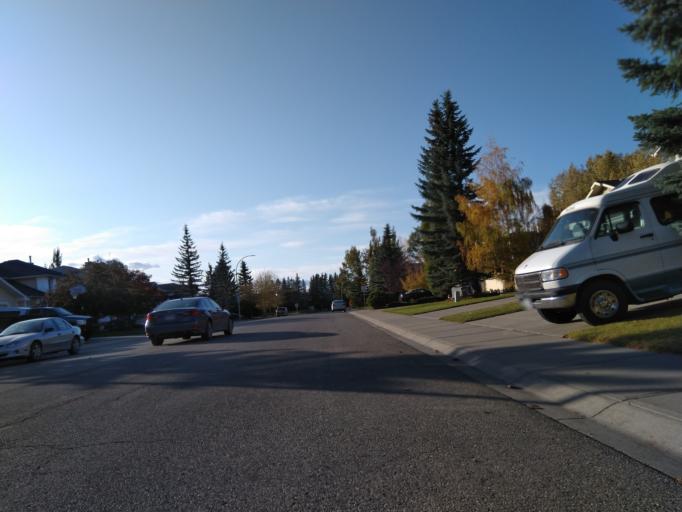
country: CA
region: Alberta
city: Cochrane
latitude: 51.1794
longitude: -114.4761
